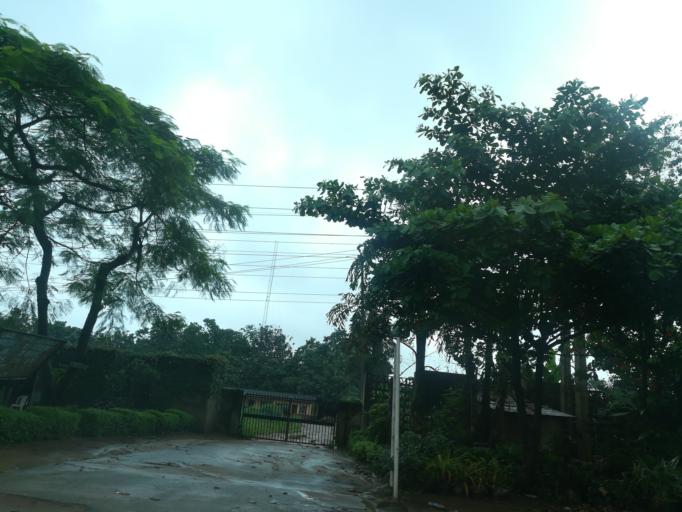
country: NG
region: Lagos
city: Ikorodu
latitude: 6.6495
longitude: 3.5183
